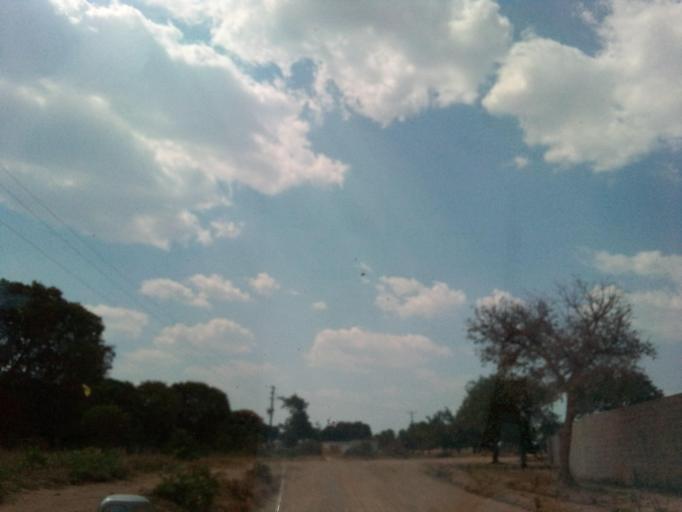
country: ZM
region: Northern
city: Mpika
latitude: -11.8379
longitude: 31.3838
